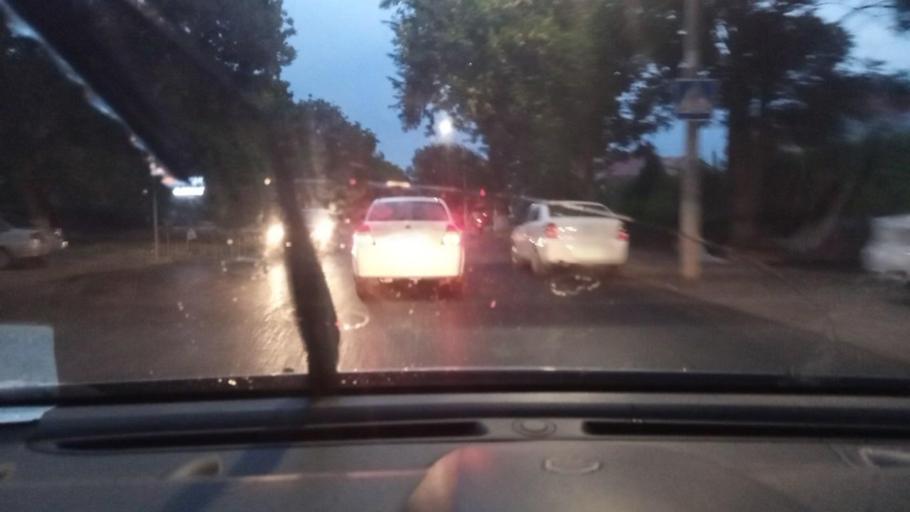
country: UZ
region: Toshkent
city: Salor
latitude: 41.3186
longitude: 69.3403
